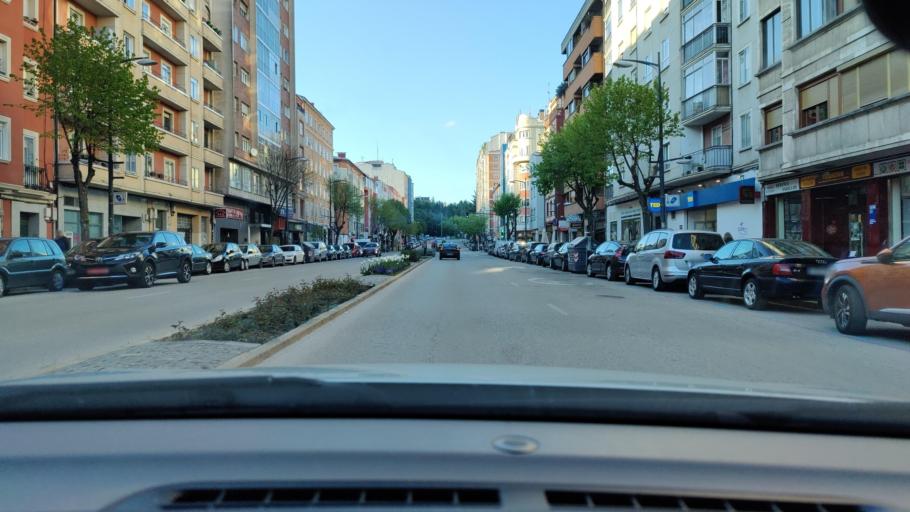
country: ES
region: Castille and Leon
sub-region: Provincia de Burgos
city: Burgos
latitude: 42.3488
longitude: -3.6966
